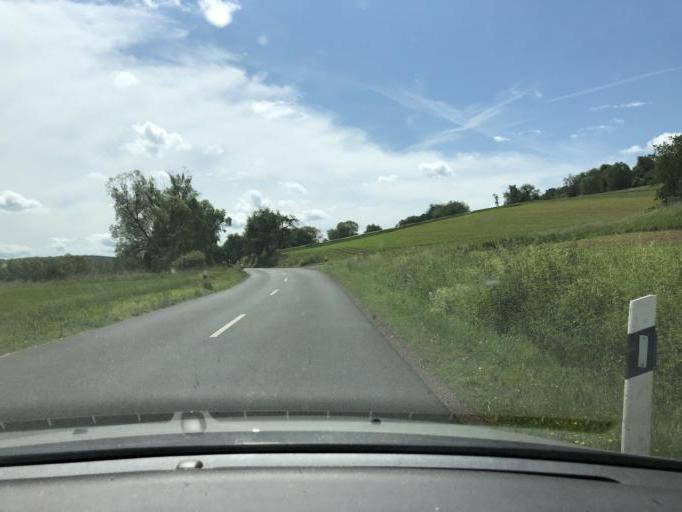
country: DE
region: Hesse
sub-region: Regierungsbezirk Kassel
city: Alheim
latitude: 51.0346
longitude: 9.6595
